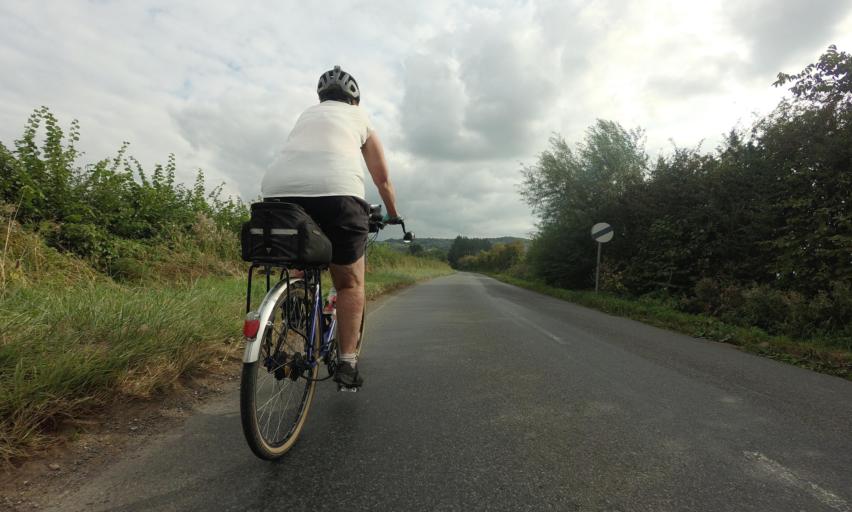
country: GB
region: England
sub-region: Gloucestershire
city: Winchcombe
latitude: 51.9814
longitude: -1.9976
